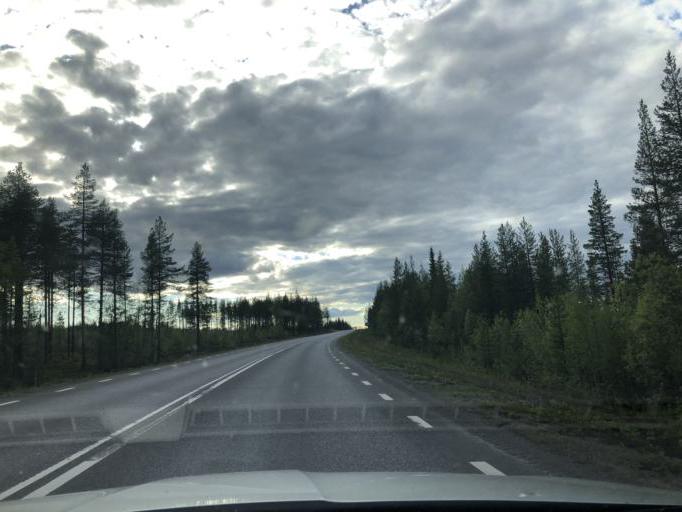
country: SE
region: Norrbotten
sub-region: Arvidsjaurs Kommun
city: Arvidsjaur
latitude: 65.6001
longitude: 19.1147
